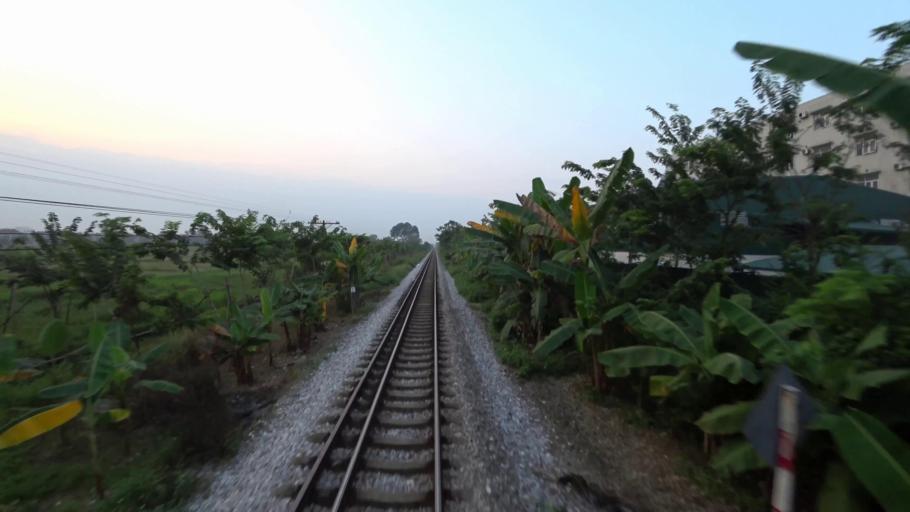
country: VN
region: Ha Noi
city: Dong Anh
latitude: 21.1438
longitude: 105.8626
